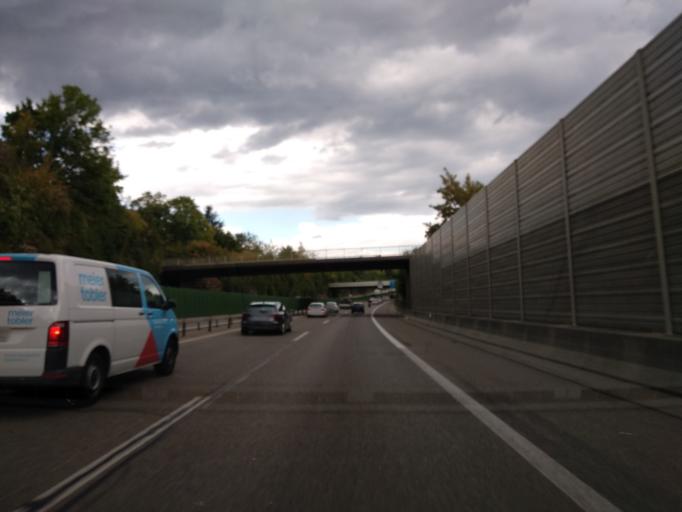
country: CH
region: Zurich
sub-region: Bezirk Winterthur
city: Wuelflingen (Kreis 6)
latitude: 47.5101
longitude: 8.6879
